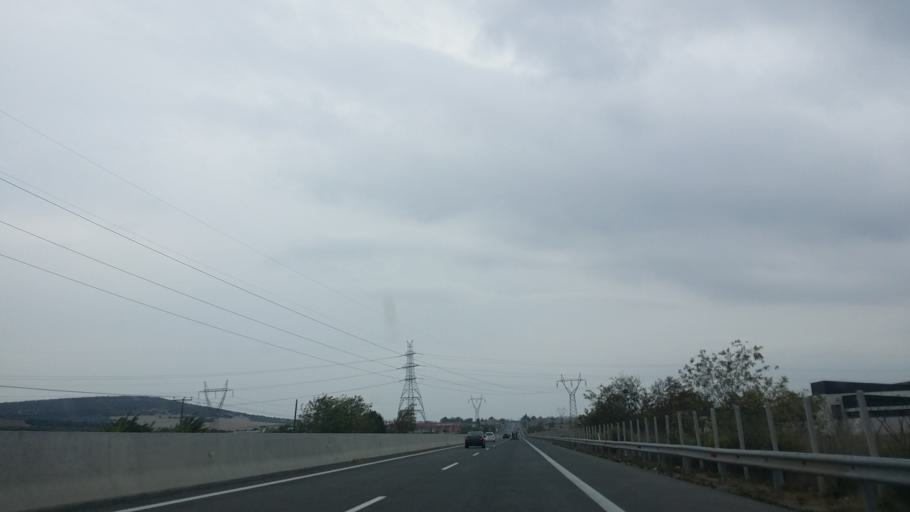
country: GR
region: Central Greece
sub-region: Nomos Voiotias
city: Arma
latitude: 38.3776
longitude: 23.4648
